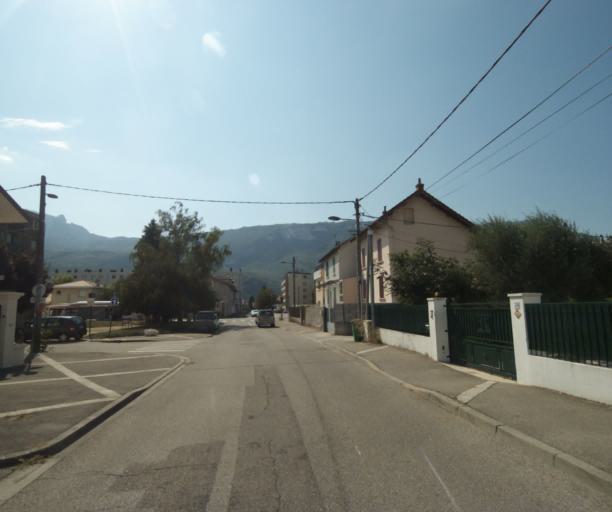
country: FR
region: Rhone-Alpes
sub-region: Departement de l'Isere
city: Fontaine
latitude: 45.1945
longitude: 5.6954
